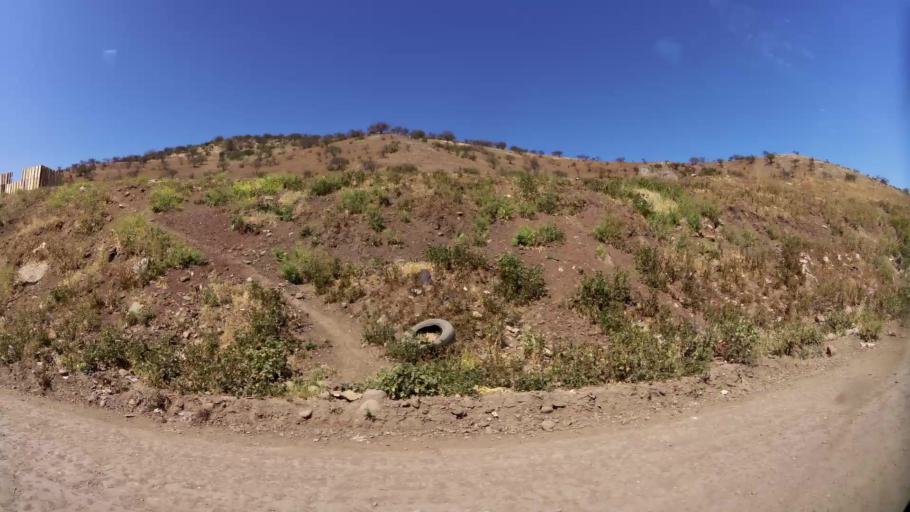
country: CL
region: Santiago Metropolitan
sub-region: Provincia de Santiago
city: Lo Prado
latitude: -33.3880
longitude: -70.7488
